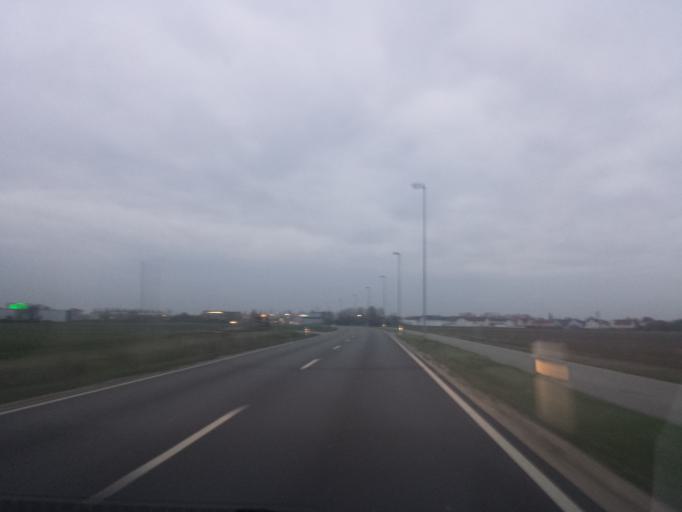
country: DE
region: Bavaria
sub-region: Upper Bavaria
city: Gaimersheim
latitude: 48.7822
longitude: 11.3887
